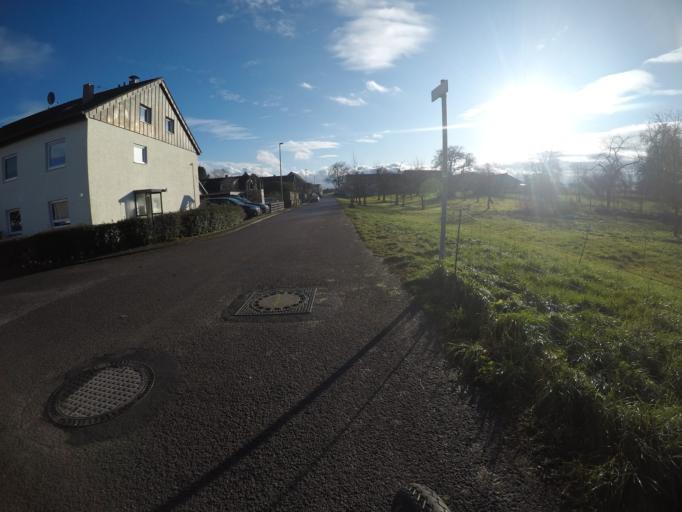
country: DE
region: Baden-Wuerttemberg
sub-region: Regierungsbezirk Stuttgart
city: Herrenberg
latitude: 48.5505
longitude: 8.8742
